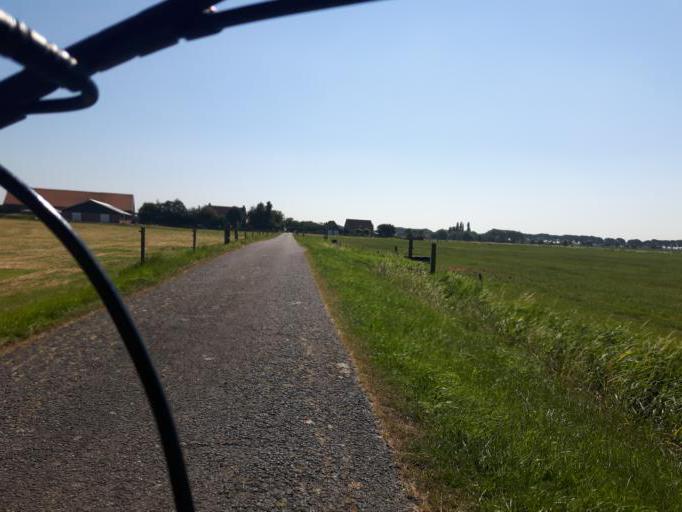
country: NL
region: Zeeland
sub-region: Gemeente Middelburg
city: Middelburg
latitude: 51.5186
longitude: 3.6400
